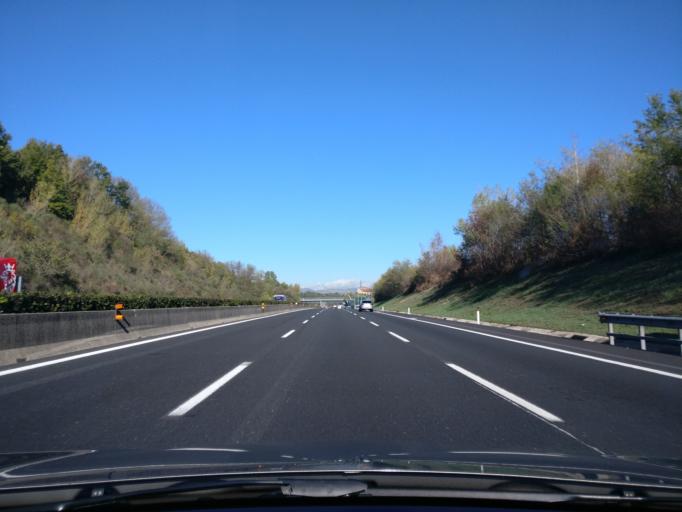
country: IT
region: Latium
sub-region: Provincia di Frosinone
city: Frosinone
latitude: 41.6058
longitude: 13.3322
